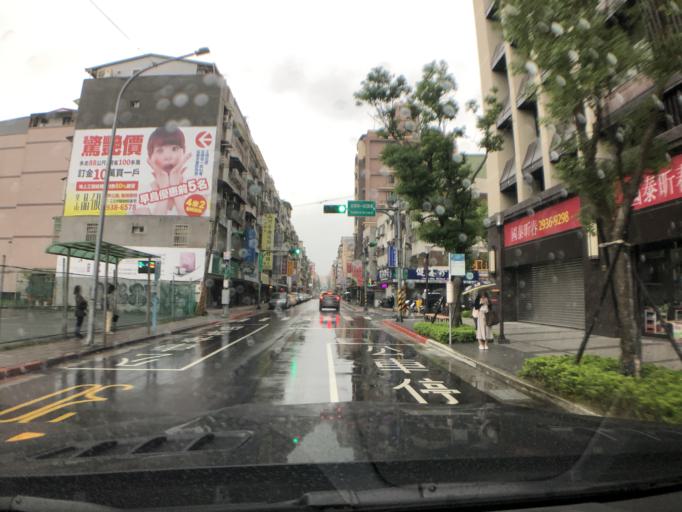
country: TW
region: Taipei
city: Taipei
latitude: 24.9840
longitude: 121.5589
